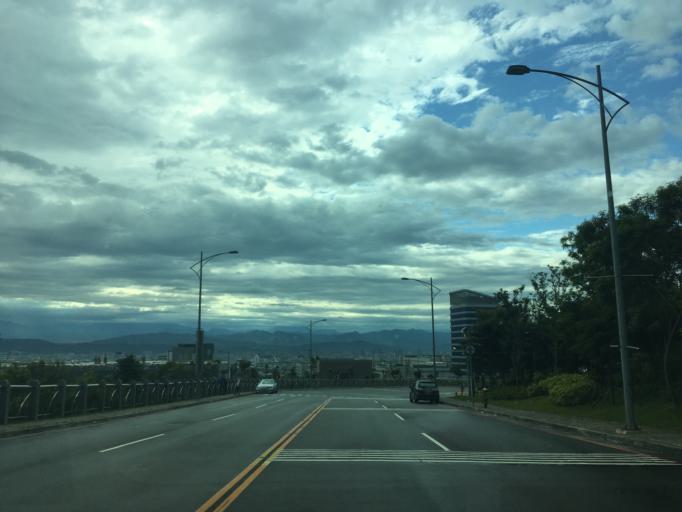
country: TW
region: Taiwan
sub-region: Taichung City
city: Taichung
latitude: 24.2123
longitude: 120.6080
